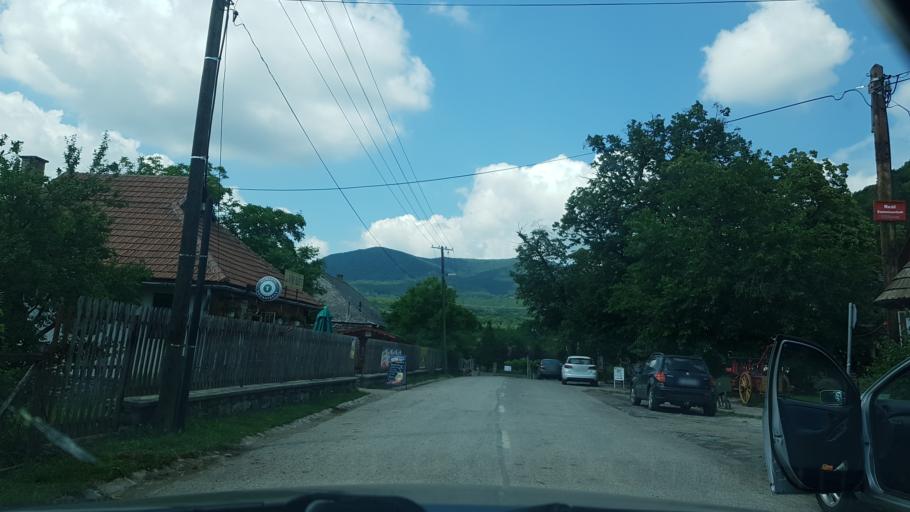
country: HU
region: Borsod-Abauj-Zemplen
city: Gonc
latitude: 48.5386
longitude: 21.4562
